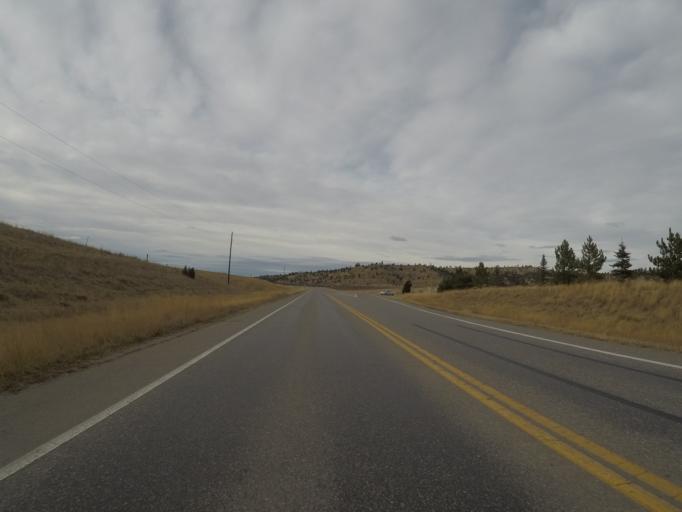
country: US
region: Montana
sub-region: Yellowstone County
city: Laurel
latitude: 45.8137
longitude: -108.6796
